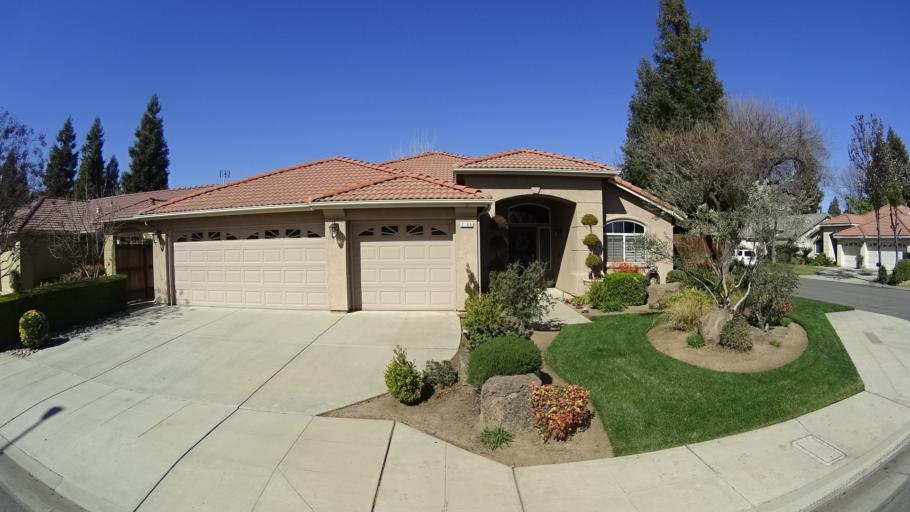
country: US
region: California
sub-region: Fresno County
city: Clovis
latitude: 36.8620
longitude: -119.7440
